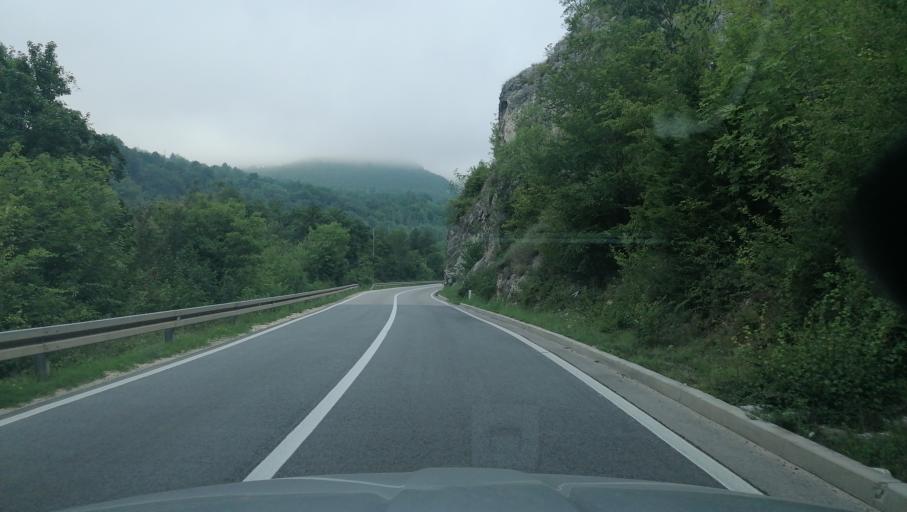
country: BA
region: Federation of Bosnia and Herzegovina
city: Divicani
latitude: 44.3712
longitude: 17.2979
